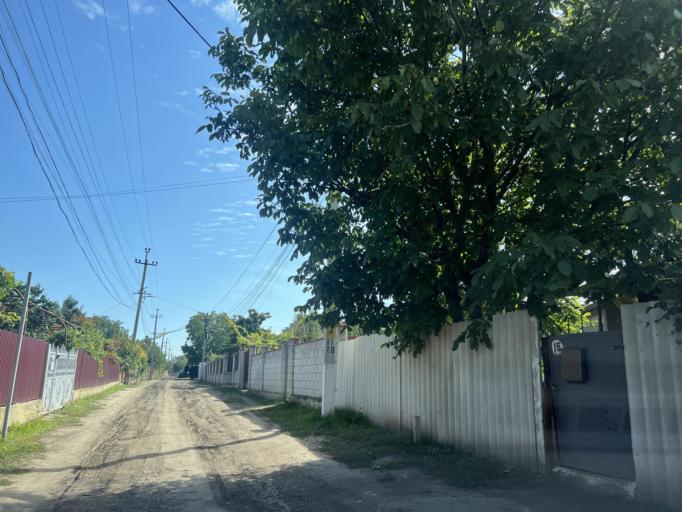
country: MD
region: Ungheni
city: Ungheni
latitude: 47.1996
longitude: 27.8137
